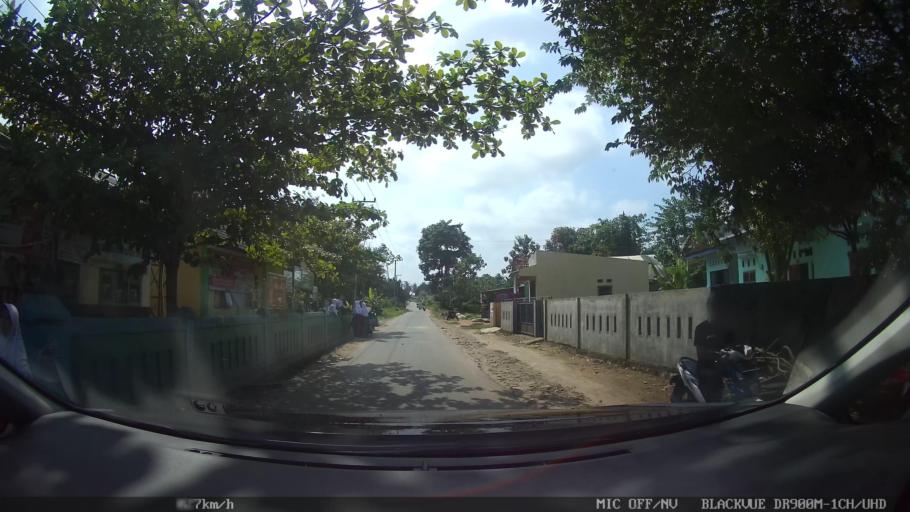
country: ID
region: Lampung
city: Kedaton
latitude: -5.3398
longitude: 105.2783
